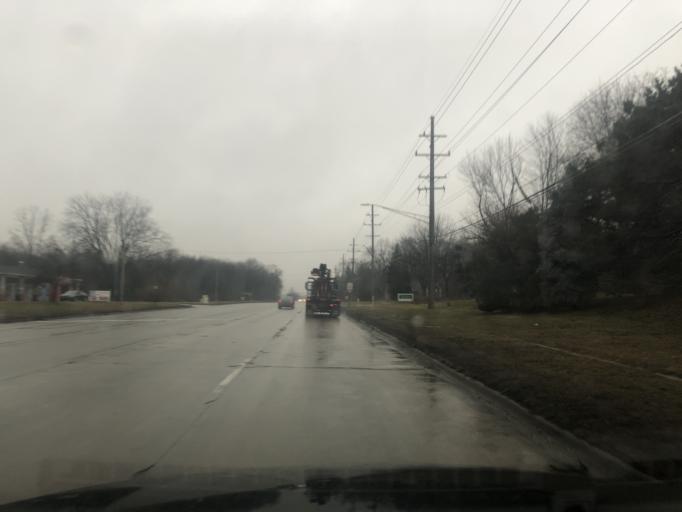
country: US
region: Michigan
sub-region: Wayne County
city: Inkster
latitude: 42.2676
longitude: -83.3413
